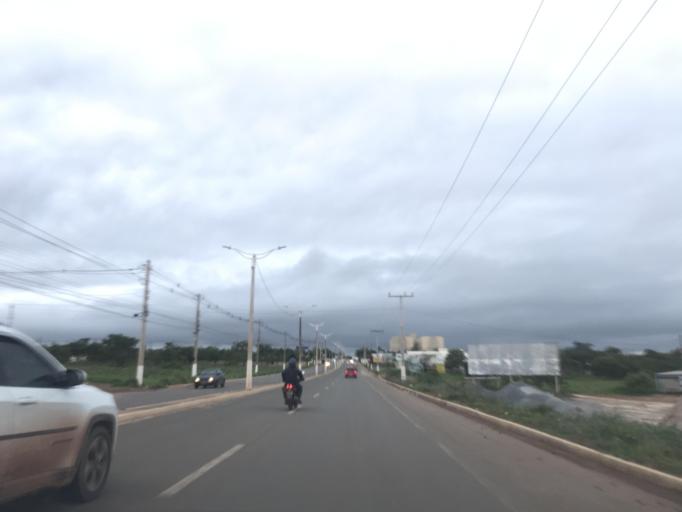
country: BR
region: Goias
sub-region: Luziania
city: Luziania
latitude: -16.2318
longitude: -47.9399
